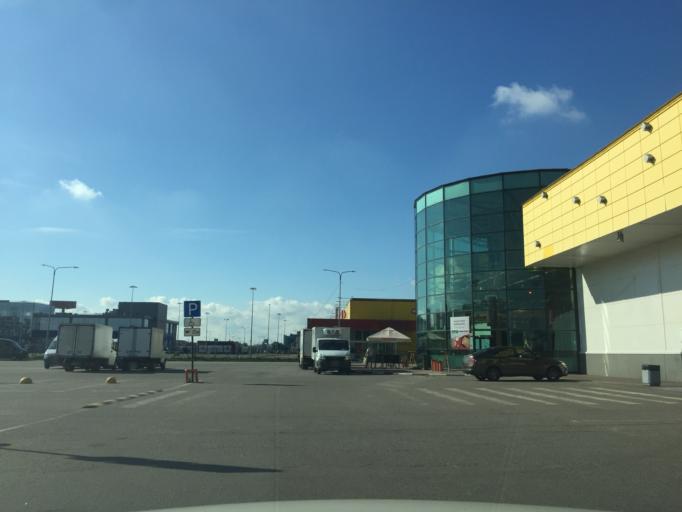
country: RU
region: St.-Petersburg
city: Kupchino
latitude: 59.8274
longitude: 30.3173
